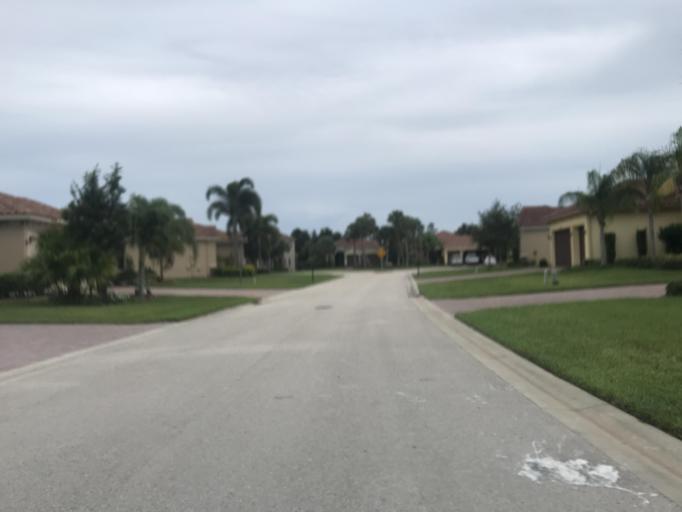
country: US
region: Florida
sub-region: Indian River County
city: Winter Beach
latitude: 27.6951
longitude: -80.4372
